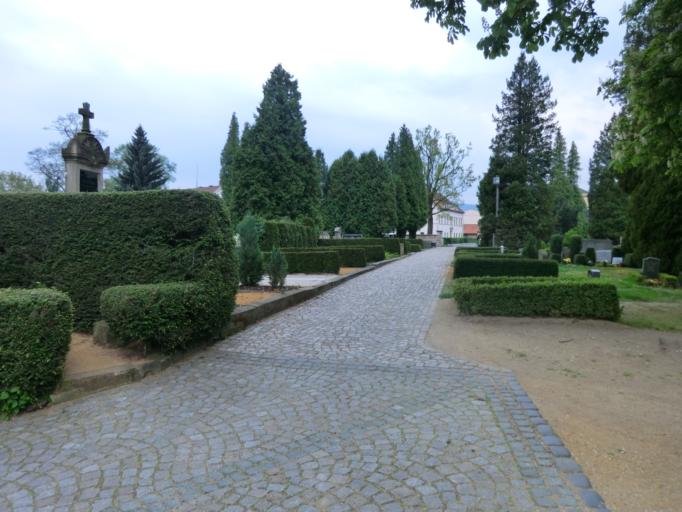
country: DE
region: Saxony
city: Grossschonau
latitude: 50.8986
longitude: 14.6626
